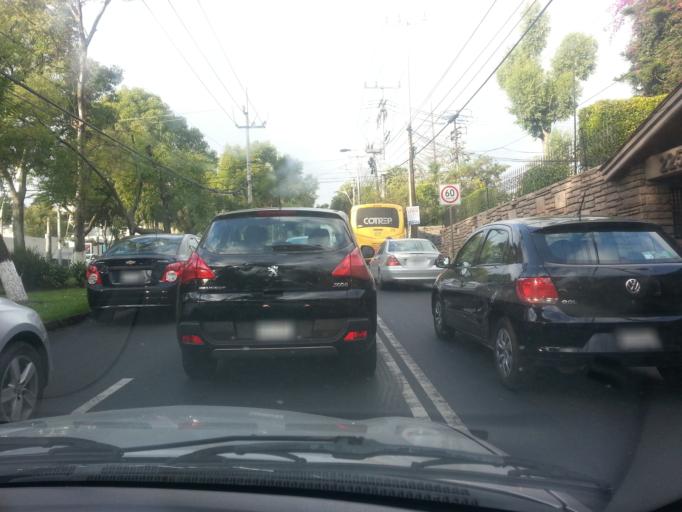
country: MX
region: Mexico City
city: Polanco
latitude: 19.4036
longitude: -99.2306
